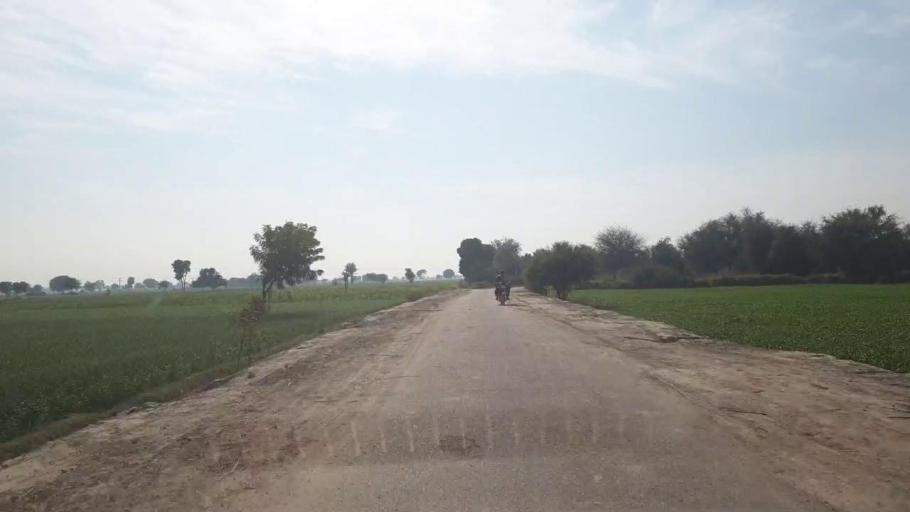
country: PK
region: Sindh
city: Shahpur Chakar
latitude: 26.1527
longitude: 68.5151
